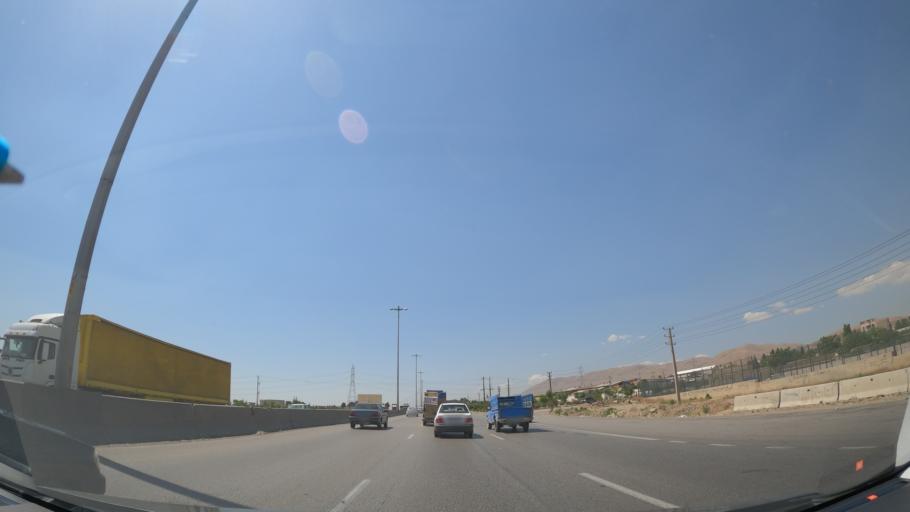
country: IR
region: Alborz
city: Karaj
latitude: 35.8684
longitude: 50.9000
